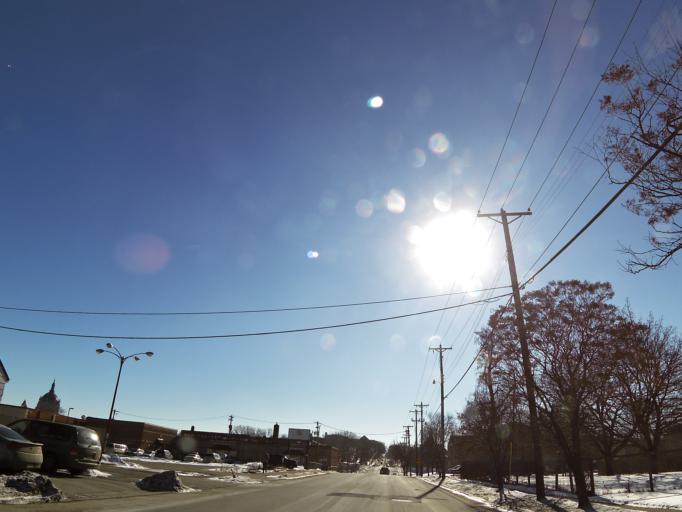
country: US
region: Minnesota
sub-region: Ramsey County
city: Saint Paul
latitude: 44.9539
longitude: -93.1161
